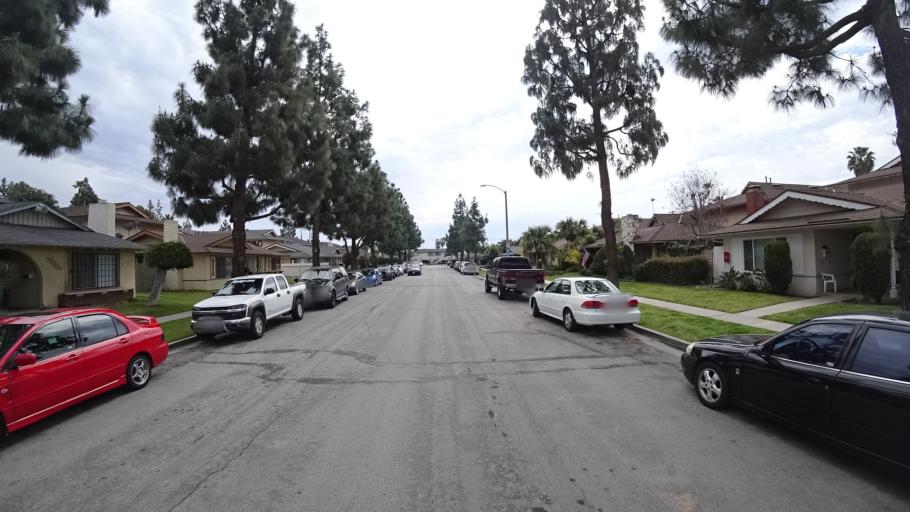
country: US
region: California
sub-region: Orange County
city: Anaheim
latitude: 33.7975
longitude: -117.9016
